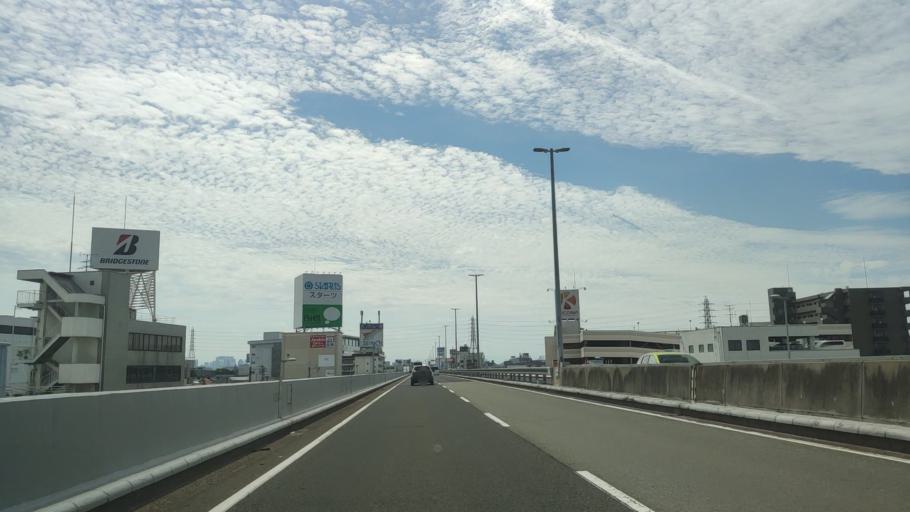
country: JP
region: Osaka
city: Toyonaka
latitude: 34.7600
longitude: 135.4618
